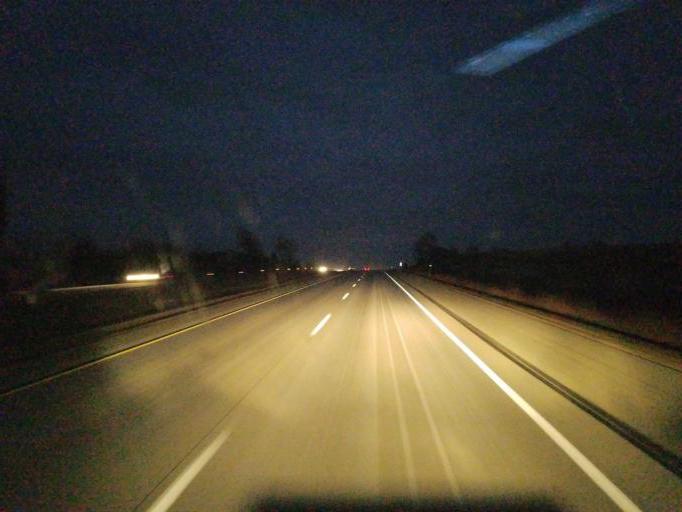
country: US
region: Iowa
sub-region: Guthrie County
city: Stuart
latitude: 41.4960
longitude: -94.4981
